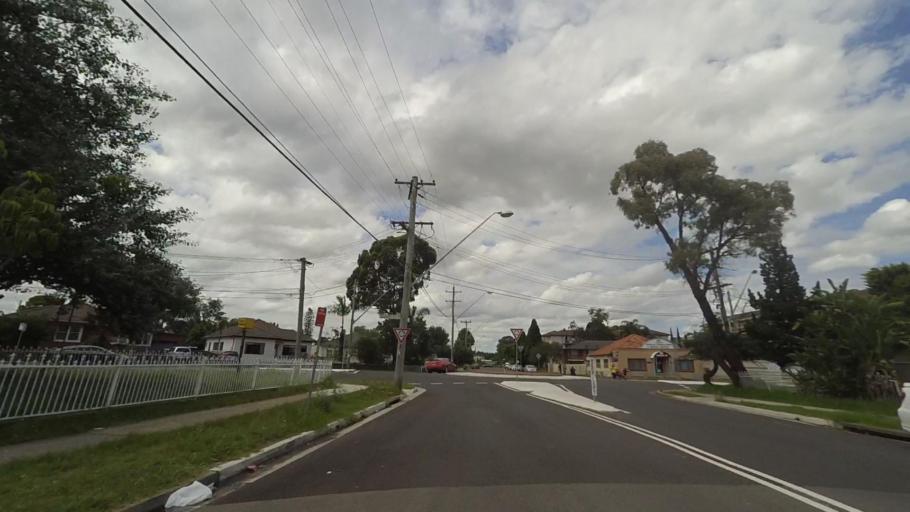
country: AU
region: New South Wales
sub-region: Fairfield
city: Fairfield Heights
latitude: -33.8659
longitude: 150.9534
